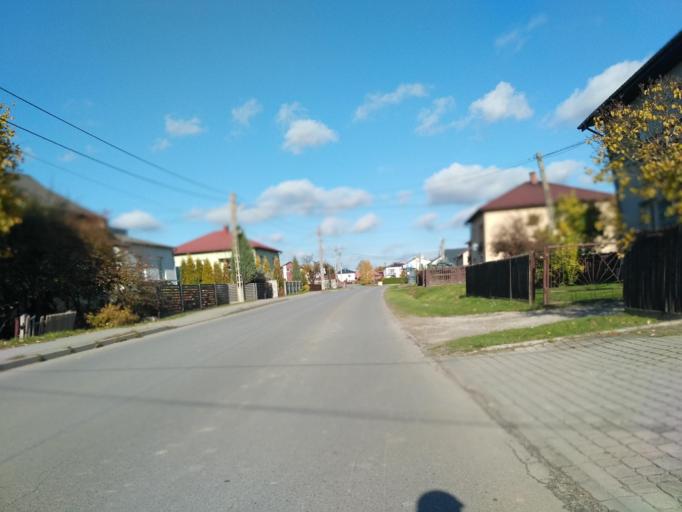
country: PL
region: Subcarpathian Voivodeship
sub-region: Powiat rzeszowski
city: Glogow Malopolski
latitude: 50.1506
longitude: 21.9123
